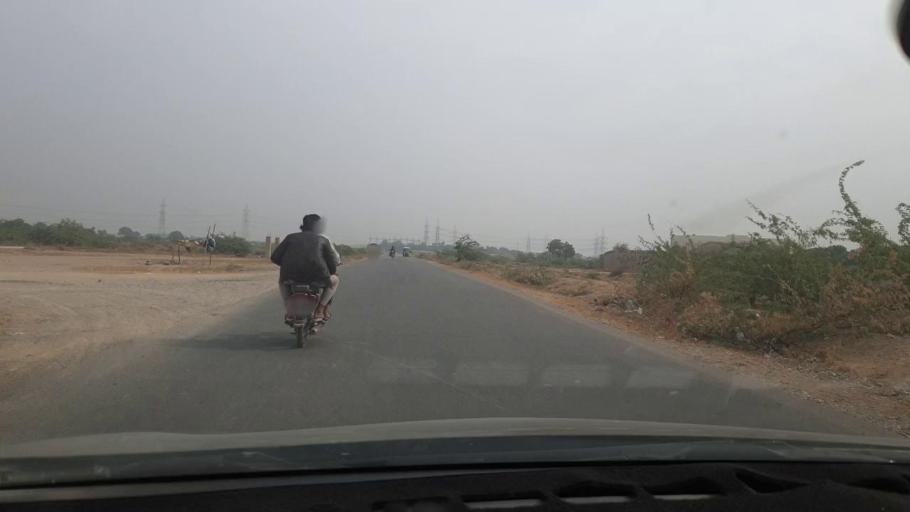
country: PK
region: Sindh
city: Malir Cantonment
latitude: 24.9134
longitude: 67.2742
